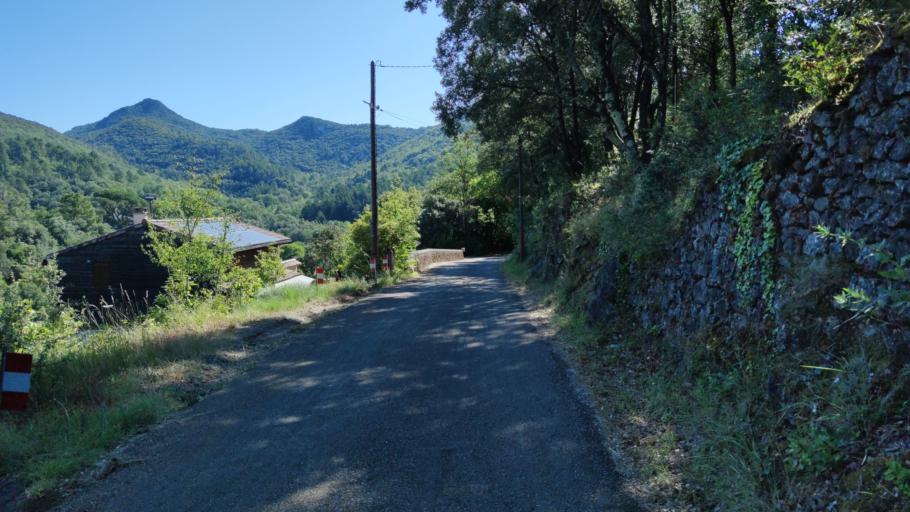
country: FR
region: Languedoc-Roussillon
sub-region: Departement du Gard
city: Saint-Hippolyte-du-Fort
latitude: 43.9744
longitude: 3.8463
